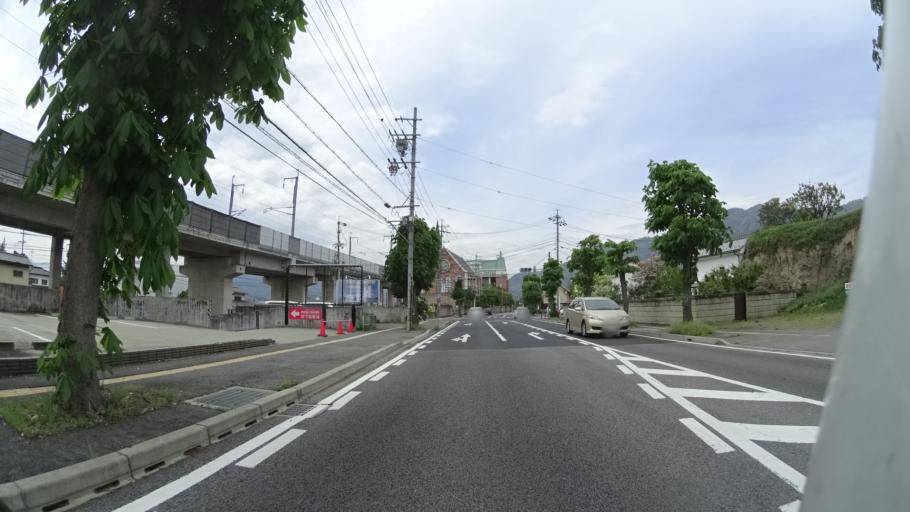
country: JP
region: Nagano
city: Ueda
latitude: 36.4045
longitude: 138.2384
